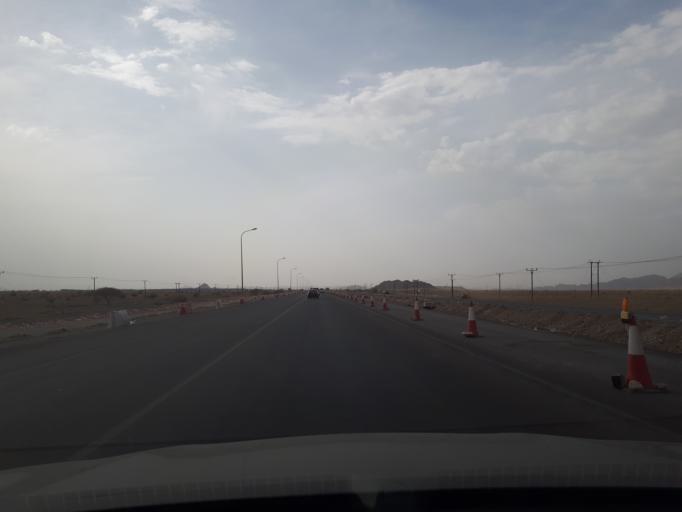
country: OM
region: Ash Sharqiyah
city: Al Qabil
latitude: 22.5457
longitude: 58.7226
